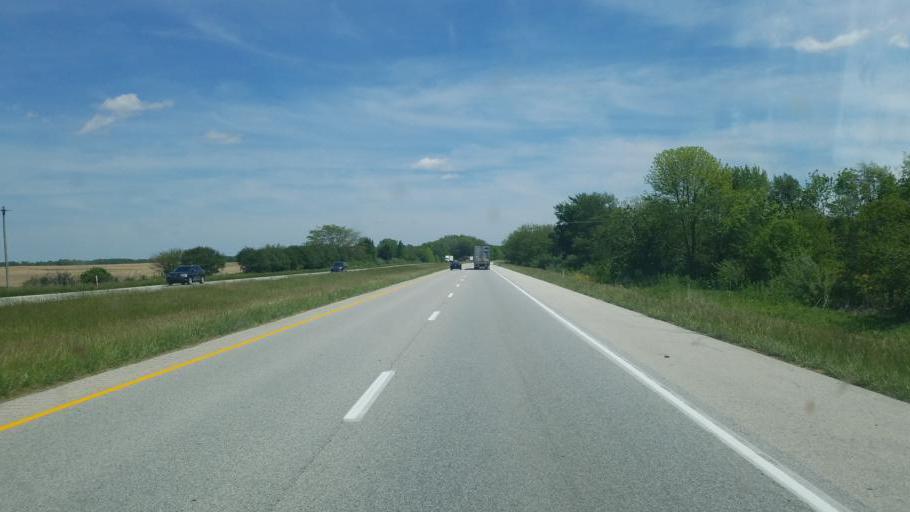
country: US
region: Indiana
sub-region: Boone County
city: Thorntown
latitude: 39.9761
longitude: -86.6684
